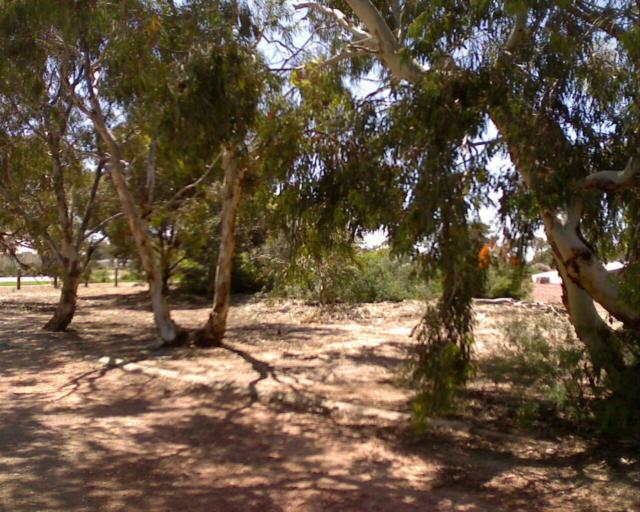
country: AU
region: South Australia
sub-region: Kimba
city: Caralue
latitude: -33.0506
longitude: 135.4615
